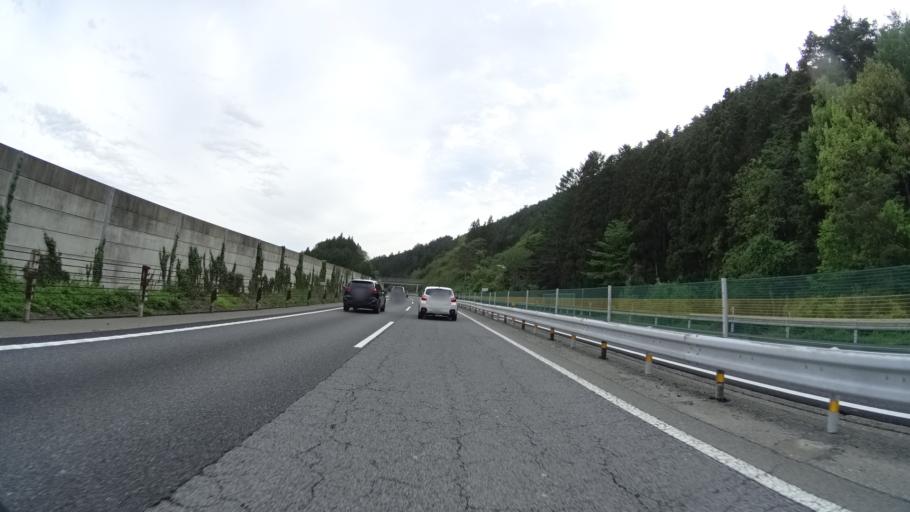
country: JP
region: Nagano
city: Ina
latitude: 35.7691
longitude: 137.9222
